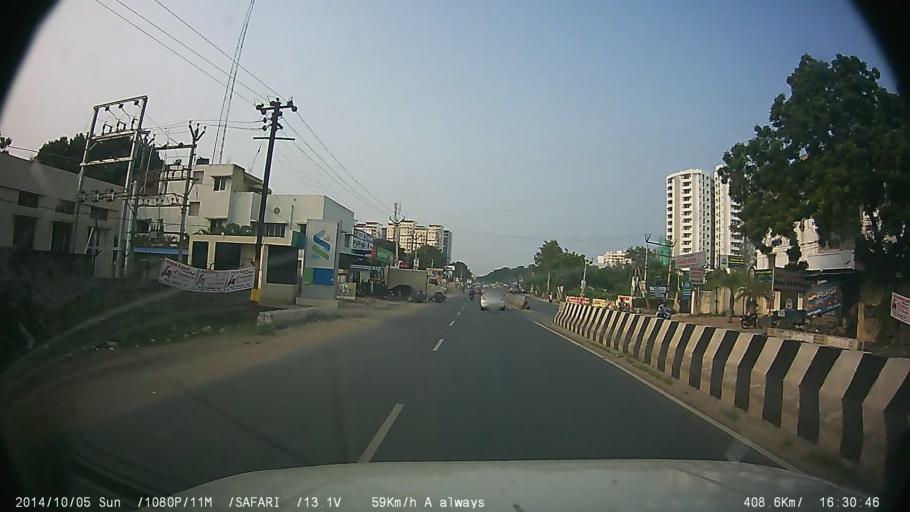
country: IN
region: Tamil Nadu
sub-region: Kancheepuram
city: Vengavasal
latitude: 12.7941
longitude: 80.2227
